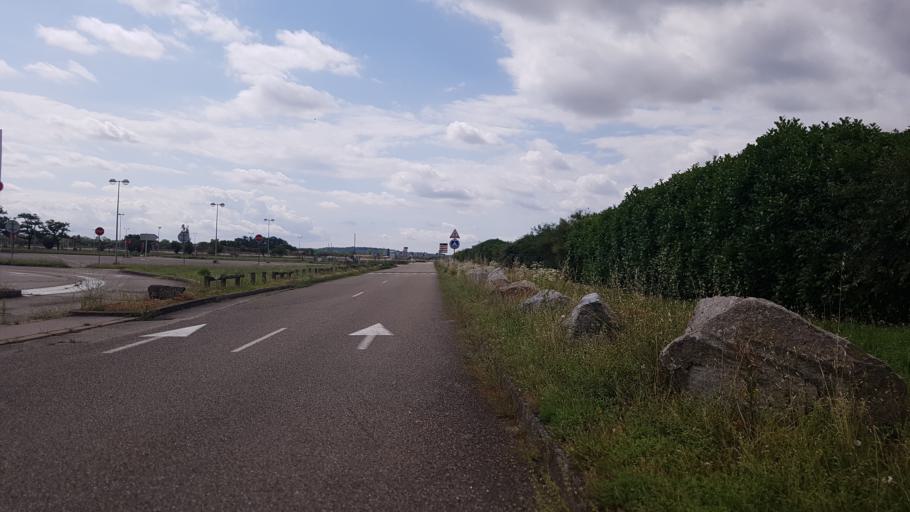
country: FR
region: Rhone-Alpes
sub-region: Departement du Rhone
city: Bron
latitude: 45.7294
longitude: 4.9460
